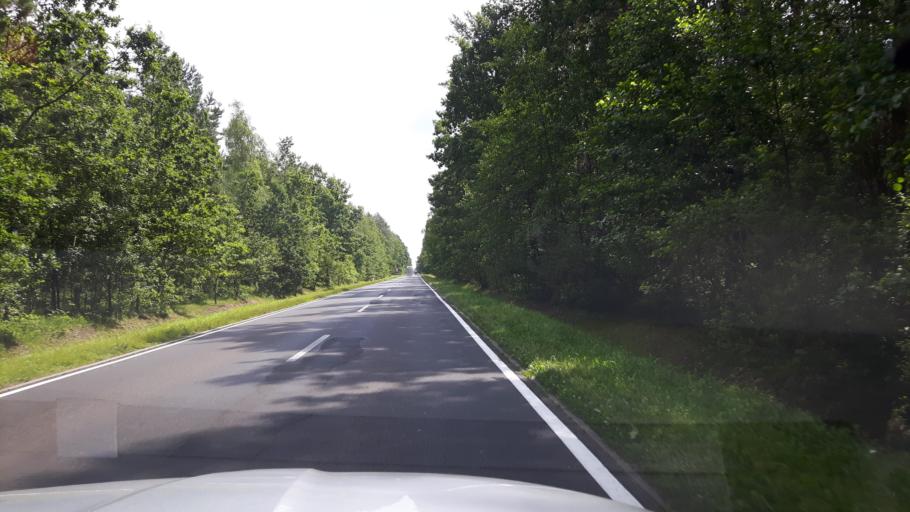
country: PL
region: Masovian Voivodeship
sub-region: Powiat ostrowski
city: Brok
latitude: 52.6983
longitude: 21.9273
